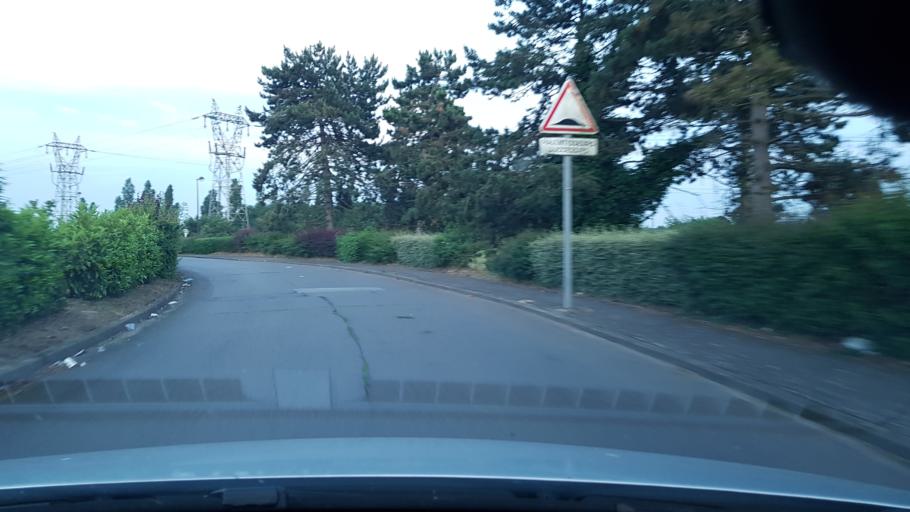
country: FR
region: Ile-de-France
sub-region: Departement de l'Essonne
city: Les Ulis
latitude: 48.6756
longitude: 2.1683
